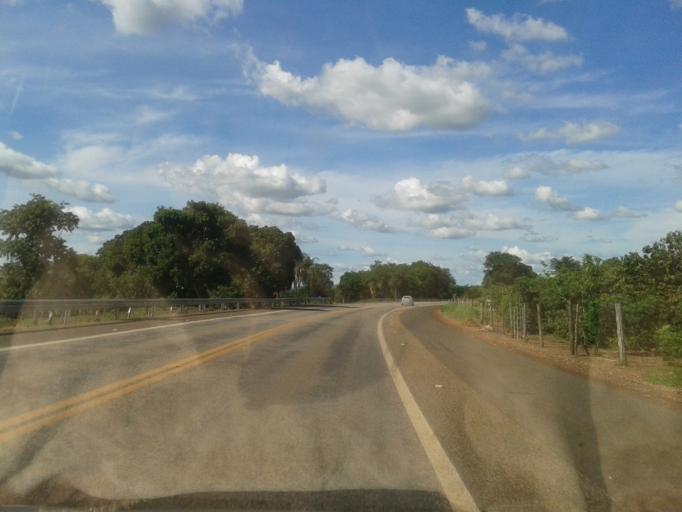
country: BR
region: Goias
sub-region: Mozarlandia
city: Mozarlandia
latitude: -15.0825
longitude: -50.6231
